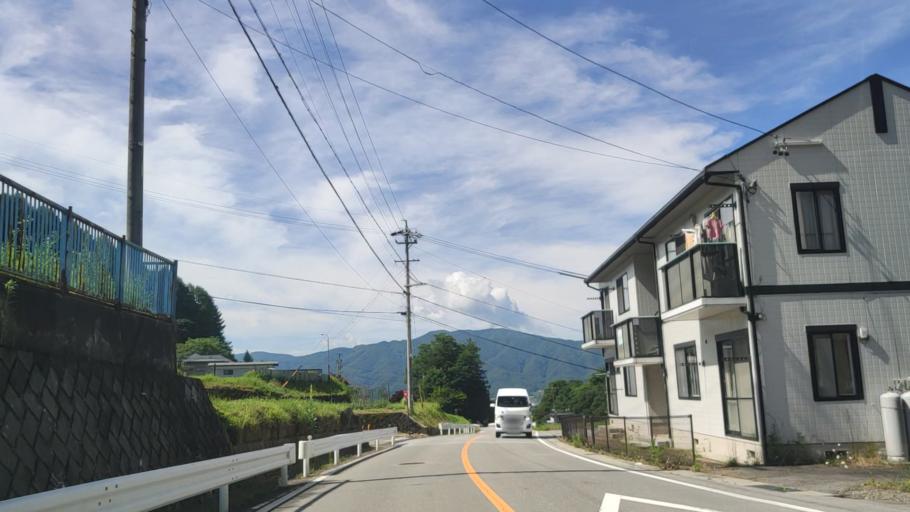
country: JP
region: Nagano
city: Suwa
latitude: 36.0515
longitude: 138.1281
